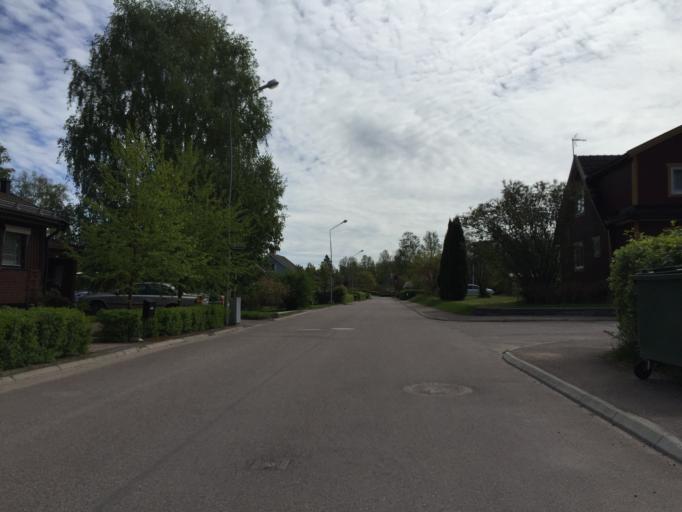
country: SE
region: Dalarna
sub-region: Ludvika Kommun
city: Ludvika
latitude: 60.1340
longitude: 15.1619
